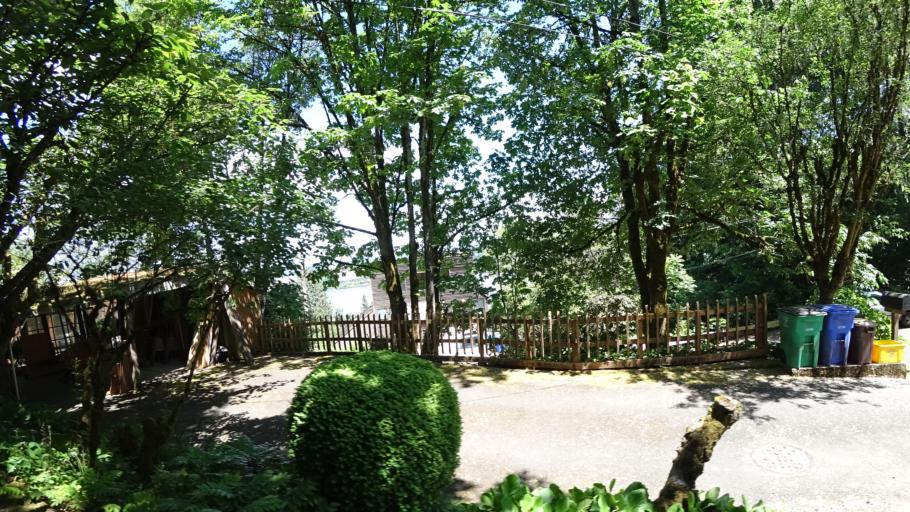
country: US
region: Oregon
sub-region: Washington County
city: Cedar Mill
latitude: 45.5967
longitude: -122.7874
